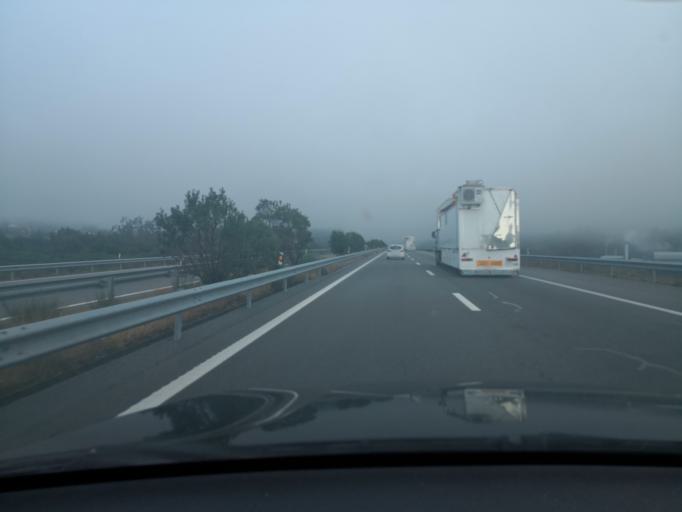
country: PT
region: Braga
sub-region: Fafe
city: Fafe
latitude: 41.4450
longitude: -8.0782
